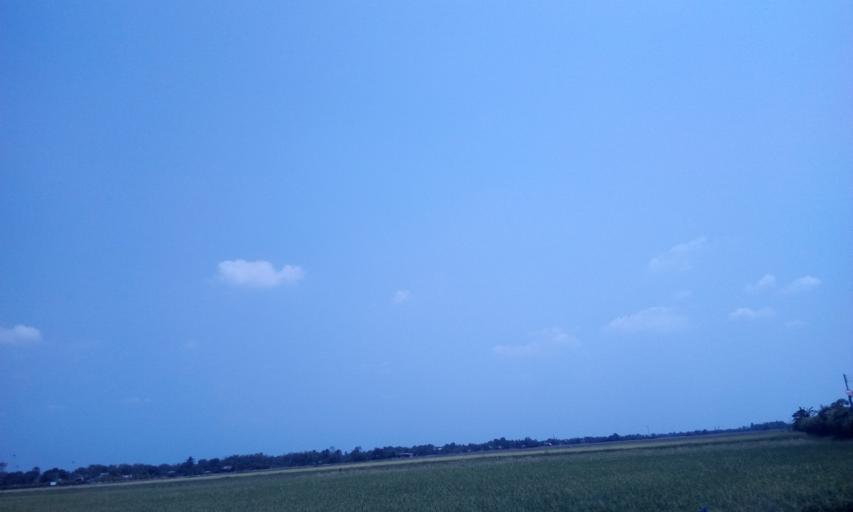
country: TH
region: Chachoengsao
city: Bang Nam Priao
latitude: 13.9637
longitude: 100.9666
